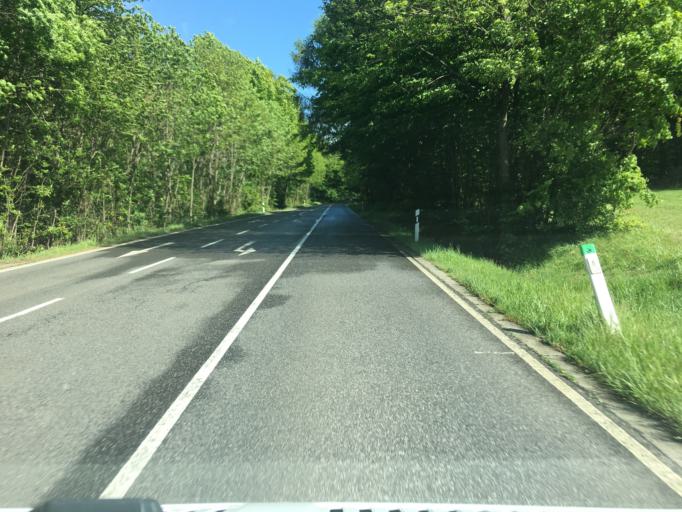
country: DE
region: North Rhine-Westphalia
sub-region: Regierungsbezirk Koln
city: Rheinbach
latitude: 50.6160
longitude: 6.9075
